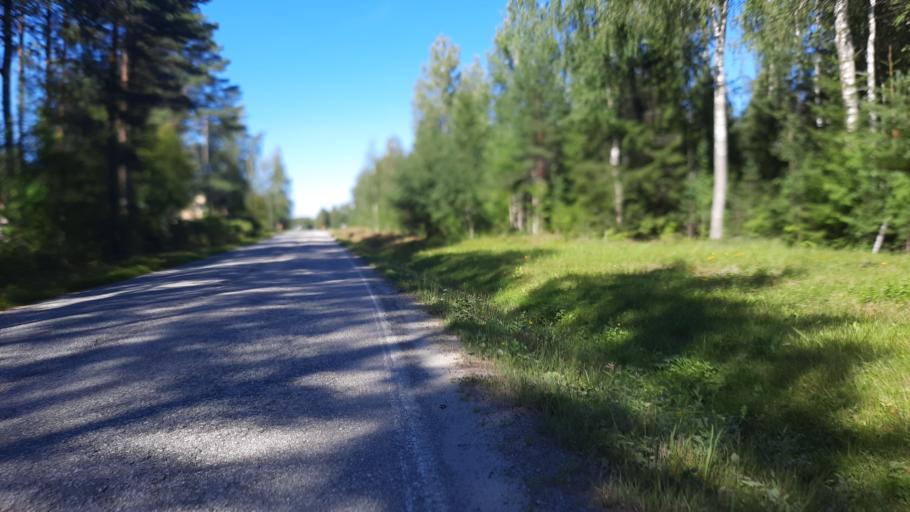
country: FI
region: North Karelia
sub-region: Joensuu
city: Joensuu
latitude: 62.6299
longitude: 29.7354
